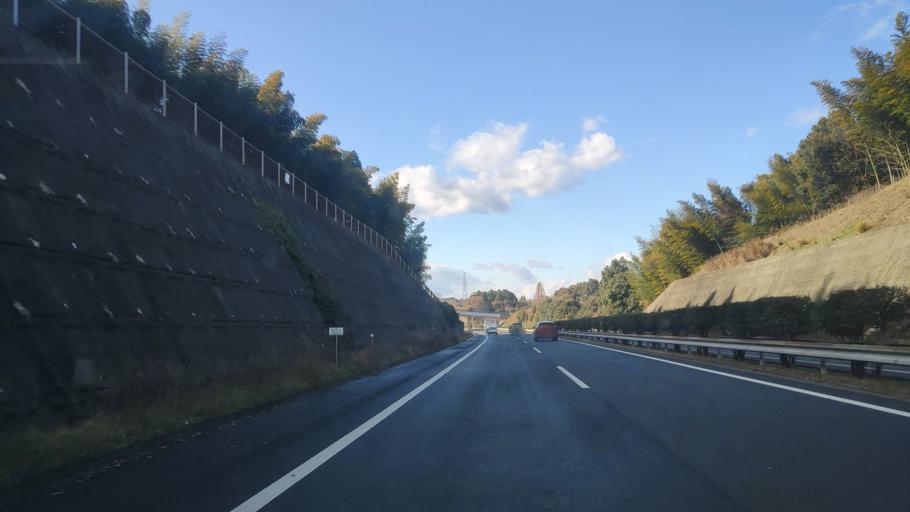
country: JP
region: Ehime
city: Saijo
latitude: 33.9101
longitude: 133.2486
